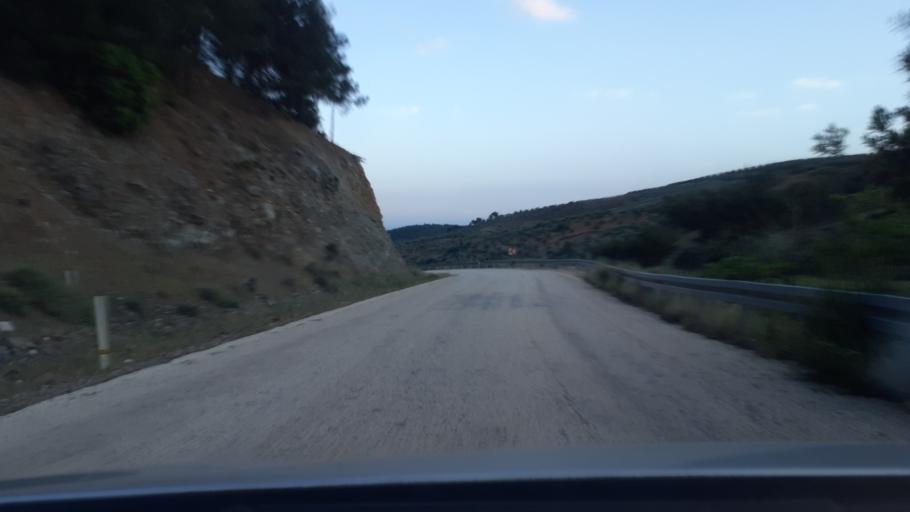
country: TR
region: Hatay
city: Kirikhan
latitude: 36.5167
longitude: 36.3186
